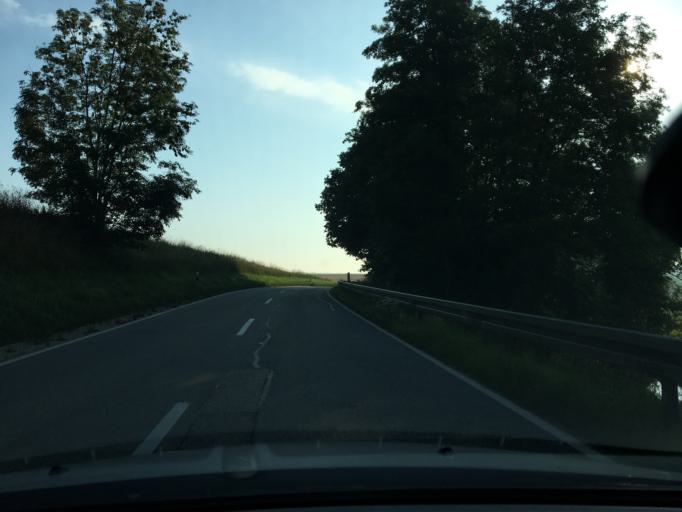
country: DE
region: Bavaria
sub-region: Lower Bavaria
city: Geisenhausen
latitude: 48.4813
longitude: 12.2868
